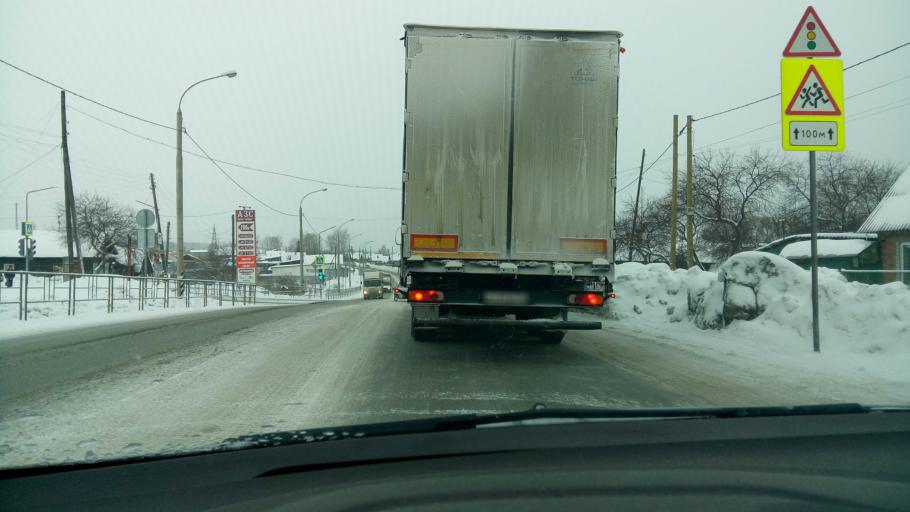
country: RU
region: Sverdlovsk
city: Beloyarskiy
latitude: 56.7567
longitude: 61.3936
